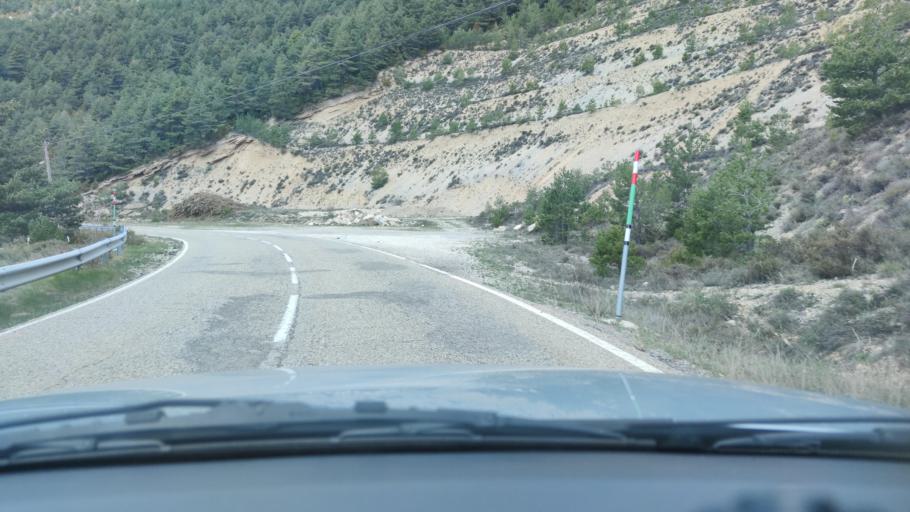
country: ES
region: Catalonia
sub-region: Provincia de Lleida
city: Gosol
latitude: 42.1520
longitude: 1.5641
